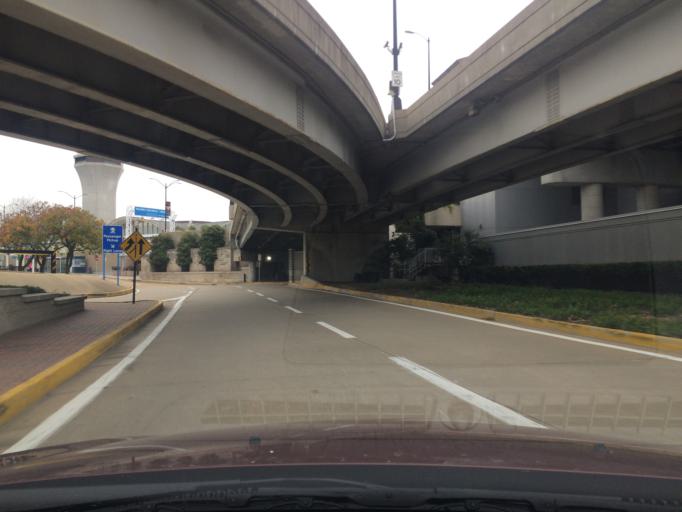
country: US
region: Missouri
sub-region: Saint Louis County
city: Woodson Terrace
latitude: 38.7409
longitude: -90.3649
